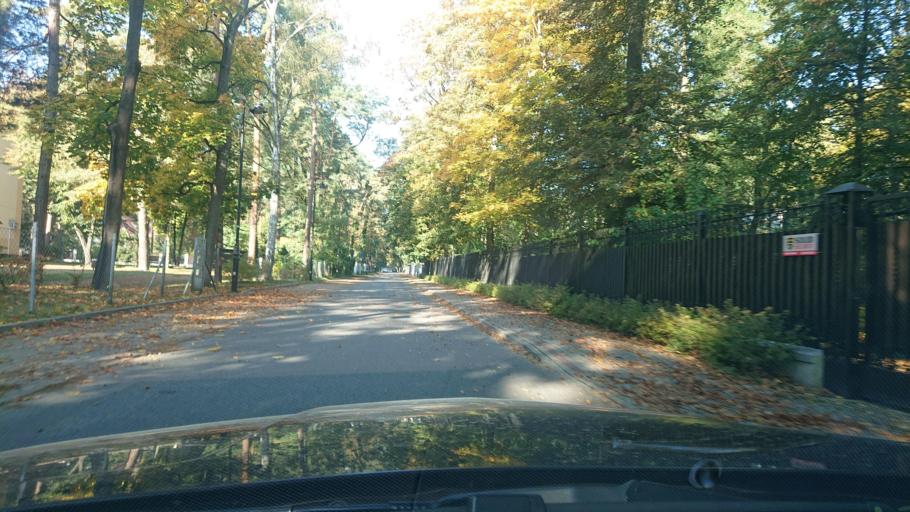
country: PL
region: Masovian Voivodeship
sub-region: Powiat piaseczynski
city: Konstancin-Jeziorna
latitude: 52.0796
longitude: 21.1242
